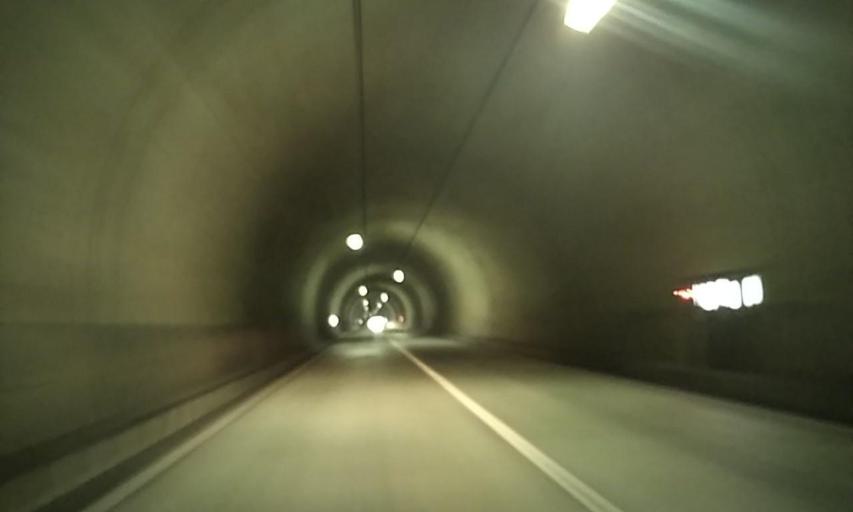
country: JP
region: Wakayama
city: Shingu
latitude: 33.8818
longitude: 135.8778
